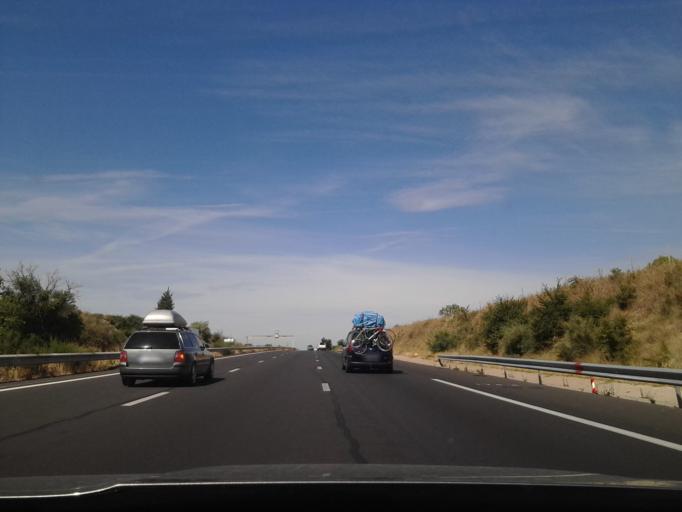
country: FR
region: Languedoc-Roussillon
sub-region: Departement de l'Aude
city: Fleury
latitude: 43.2307
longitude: 3.1200
